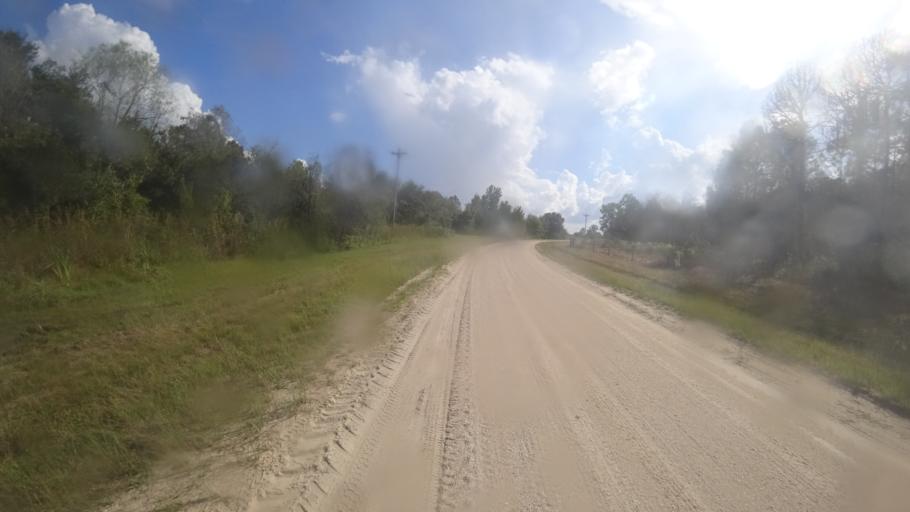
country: US
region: Florida
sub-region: Hillsborough County
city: Wimauma
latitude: 27.6047
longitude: -82.1187
